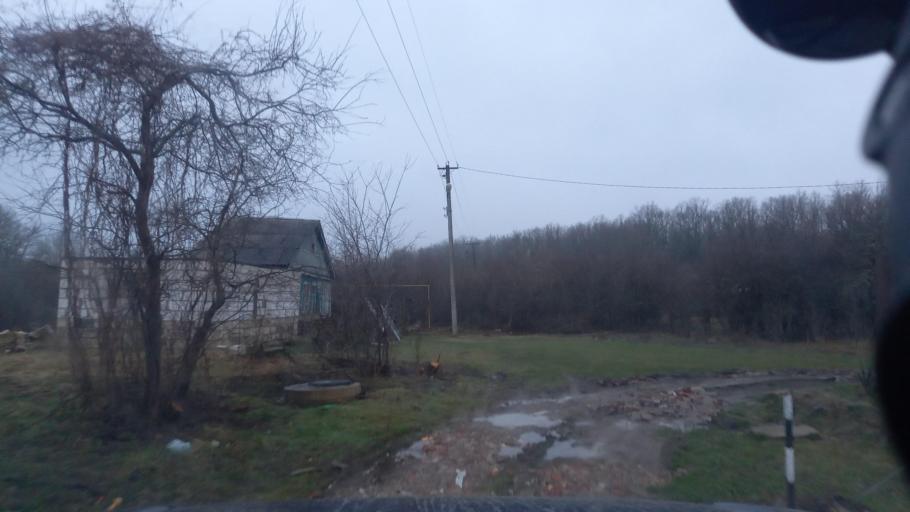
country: RU
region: Krasnodarskiy
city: Saratovskaya
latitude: 44.6451
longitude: 39.3041
